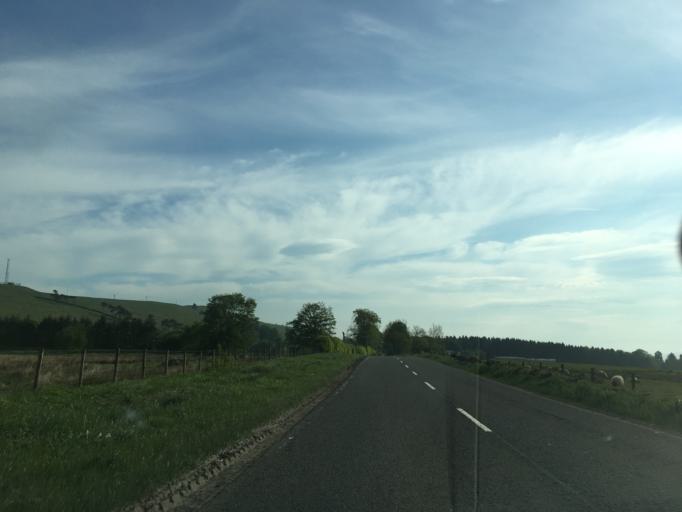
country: GB
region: Scotland
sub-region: Midlothian
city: Penicuik
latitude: 55.7598
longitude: -3.2671
